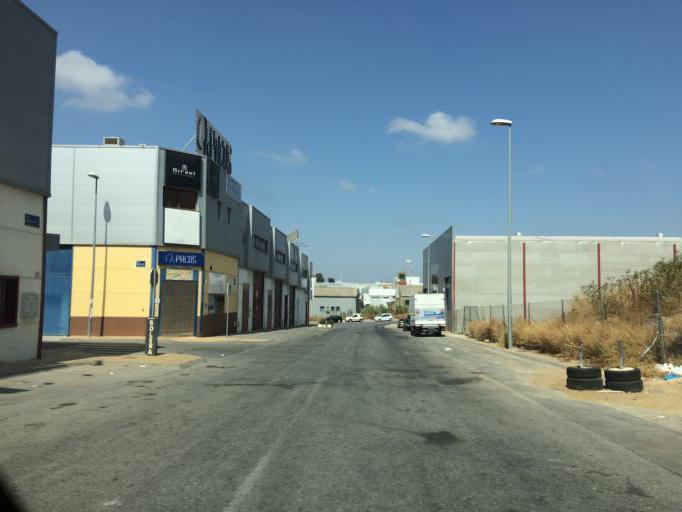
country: ES
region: Andalusia
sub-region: Provincia de Malaga
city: Malaga
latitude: 36.7115
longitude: -4.4714
